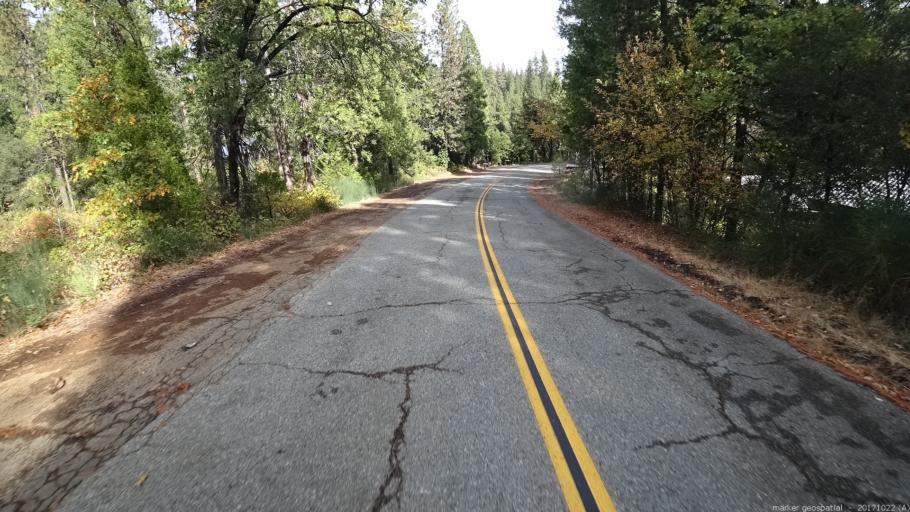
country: US
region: California
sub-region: Siskiyou County
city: Dunsmuir
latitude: 41.0729
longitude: -122.3608
